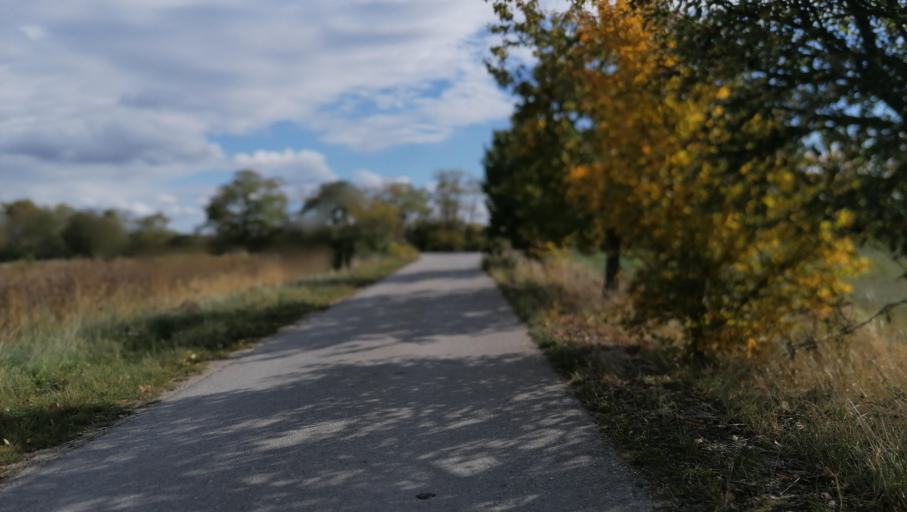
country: AT
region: Lower Austria
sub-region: Politischer Bezirk Baden
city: Tattendorf
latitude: 47.9639
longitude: 16.2959
